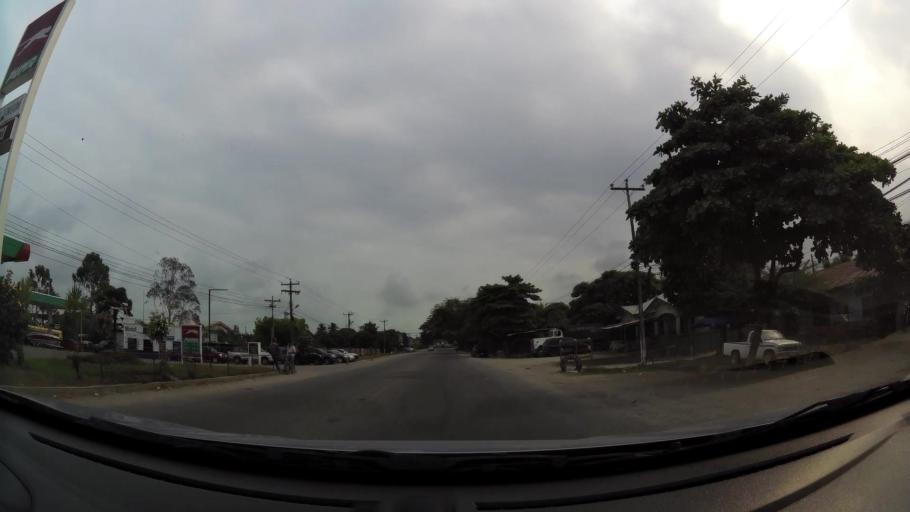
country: HN
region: Yoro
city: El Progreso
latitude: 15.4224
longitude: -87.7995
